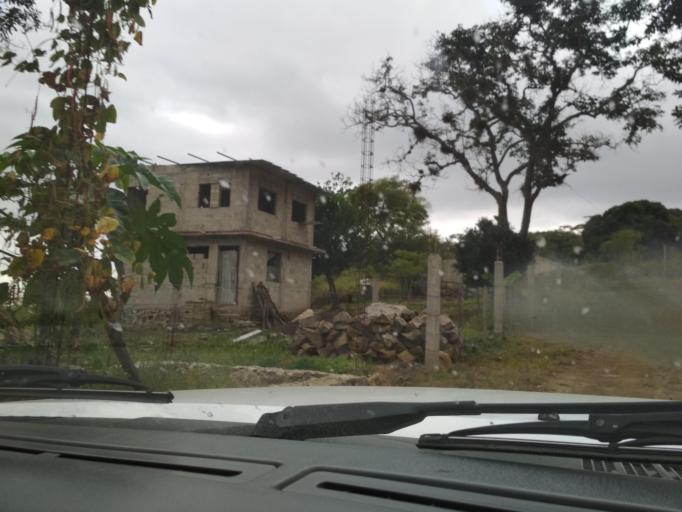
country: MX
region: Veracruz
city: El Castillo
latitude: 19.5663
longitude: -96.8484
